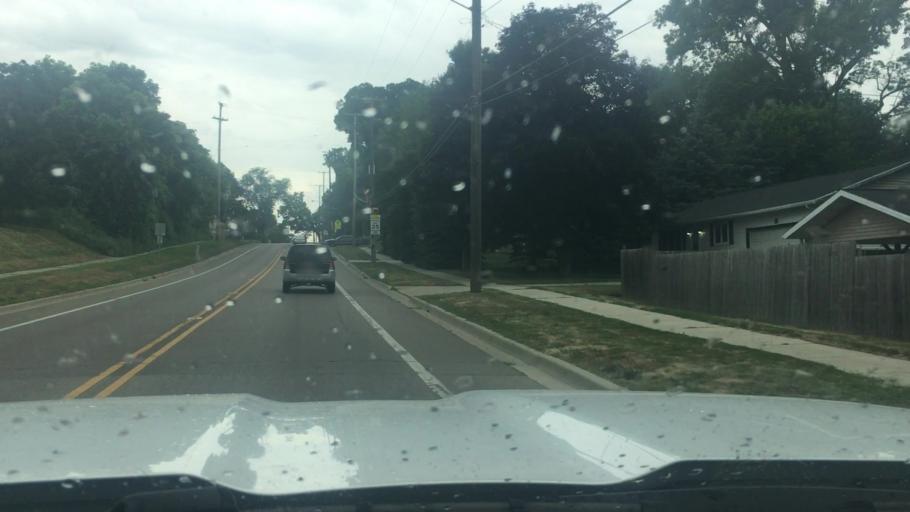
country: US
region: Michigan
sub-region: Ionia County
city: Ionia
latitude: 42.9874
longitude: -85.0607
